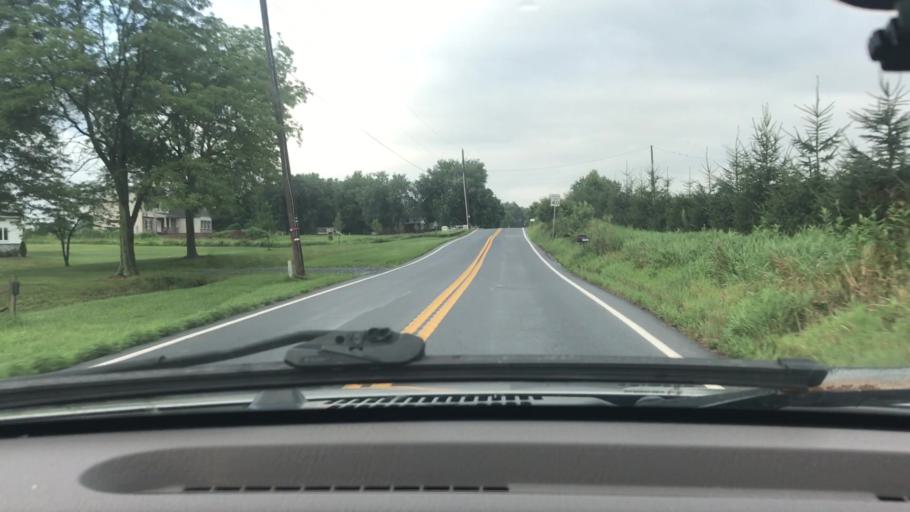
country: US
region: Pennsylvania
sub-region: Lancaster County
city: Elizabethtown
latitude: 40.2017
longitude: -76.6423
